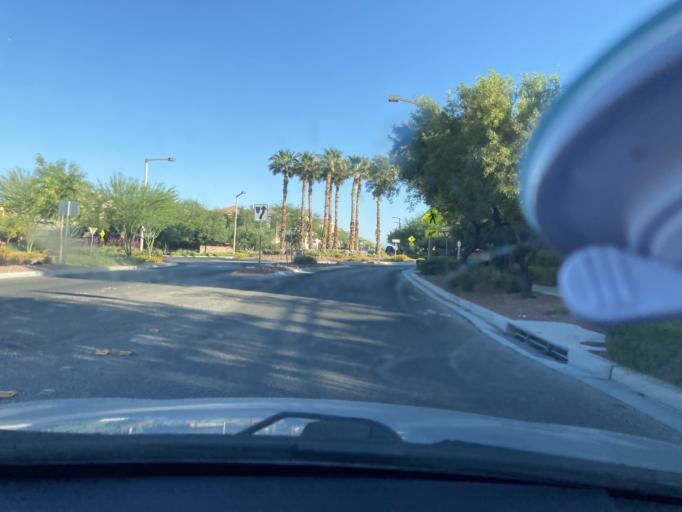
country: US
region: Nevada
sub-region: Clark County
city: Summerlin South
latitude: 36.1544
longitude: -115.3406
